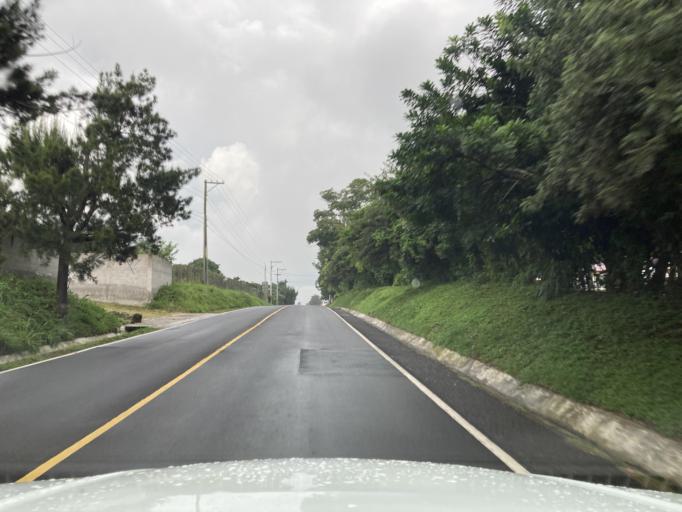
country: GT
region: Sacatepequez
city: Ciudad Vieja
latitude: 14.5198
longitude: -90.7786
